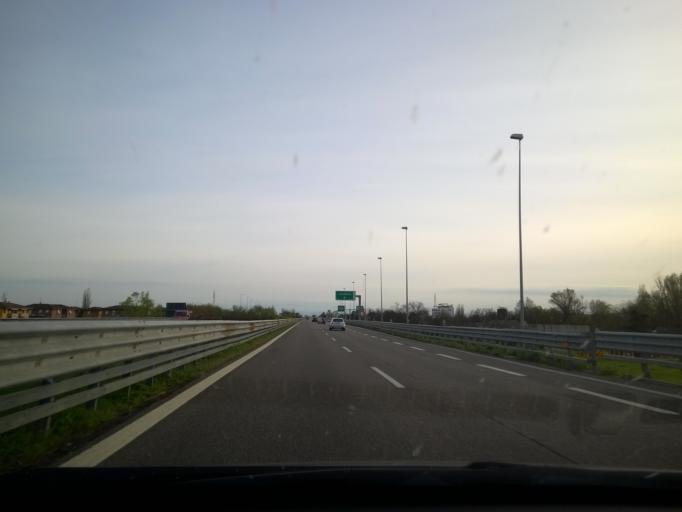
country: IT
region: Lombardy
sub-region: Provincia di Cremona
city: San Felice
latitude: 45.1446
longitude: 10.0723
